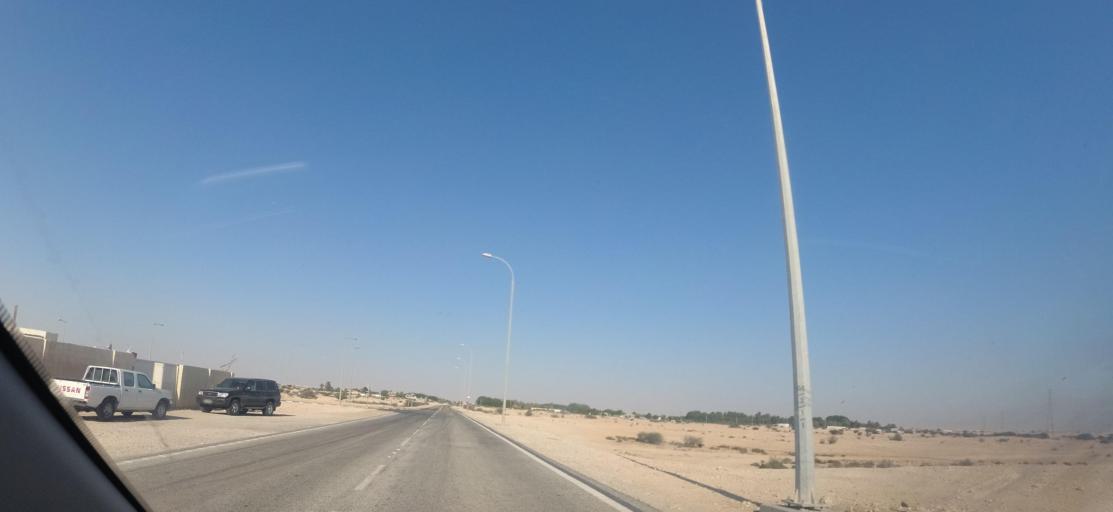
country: QA
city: Al Jumayliyah
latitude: 25.6209
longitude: 51.0869
